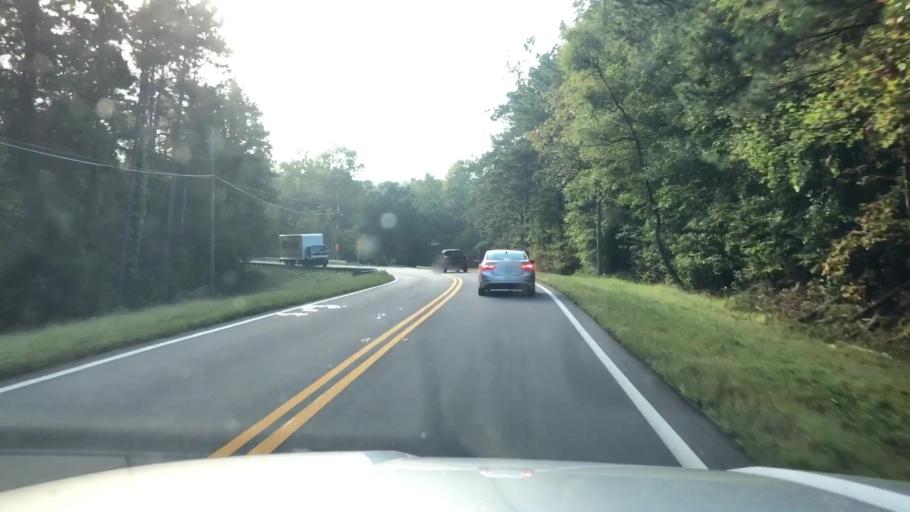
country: US
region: Georgia
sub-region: Bartow County
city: Emerson
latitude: 34.0794
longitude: -84.7561
